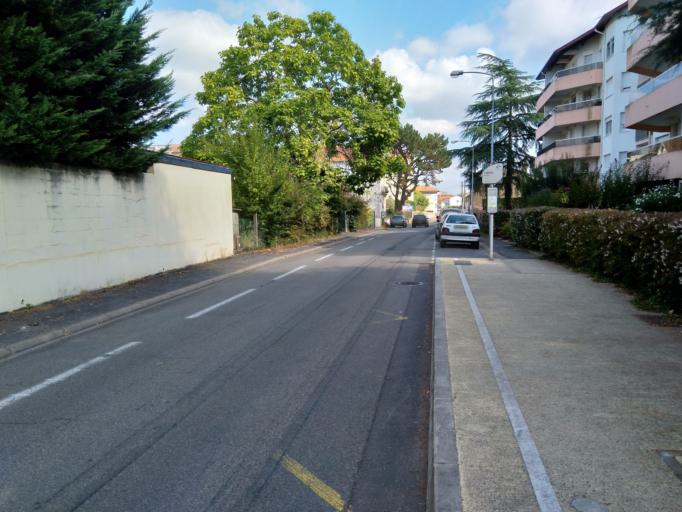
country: FR
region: Aquitaine
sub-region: Departement des Landes
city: Dax
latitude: 43.7032
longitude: -1.0617
